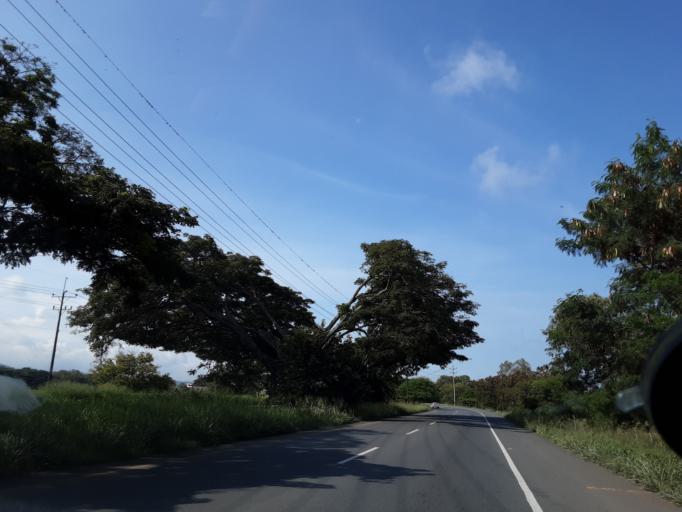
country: CO
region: Valle del Cauca
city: Buga
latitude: 3.8824
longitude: -76.3133
